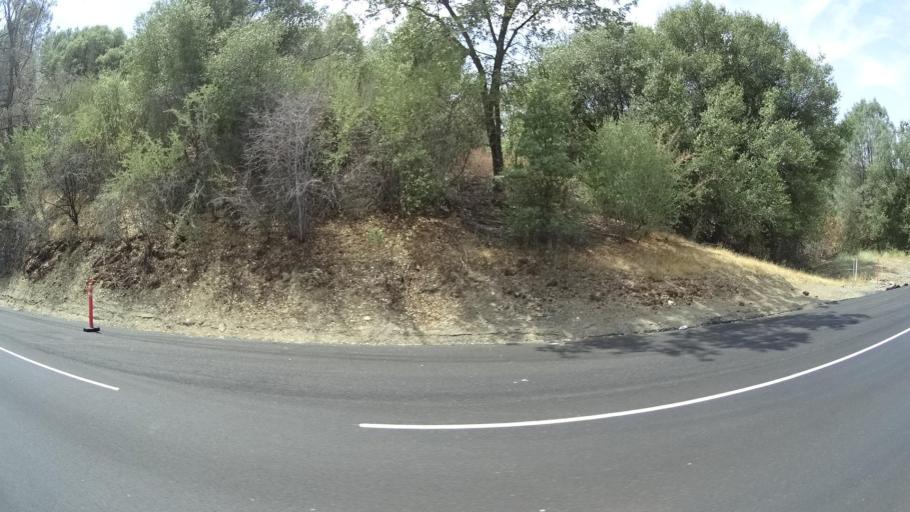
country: US
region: California
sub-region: Mariposa County
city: Midpines
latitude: 37.4472
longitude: -119.8479
